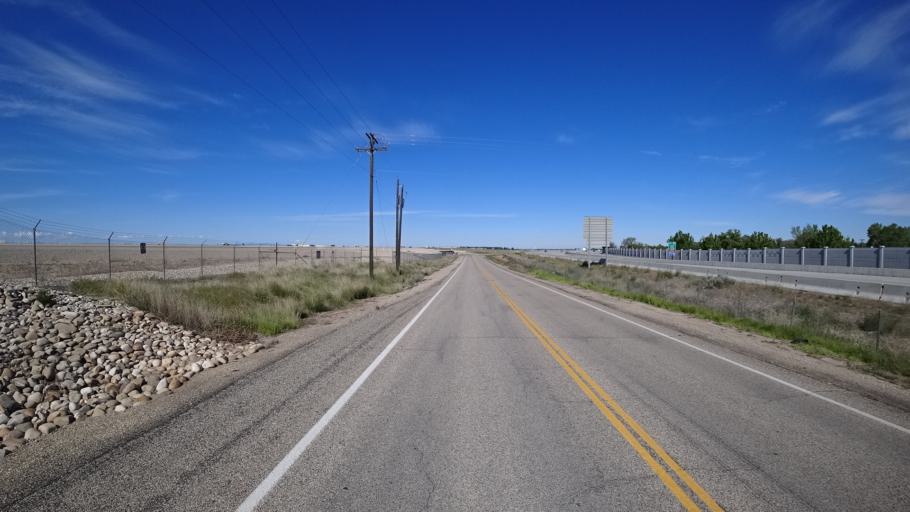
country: US
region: Idaho
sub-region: Ada County
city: Garden City
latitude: 43.5716
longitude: -116.2332
